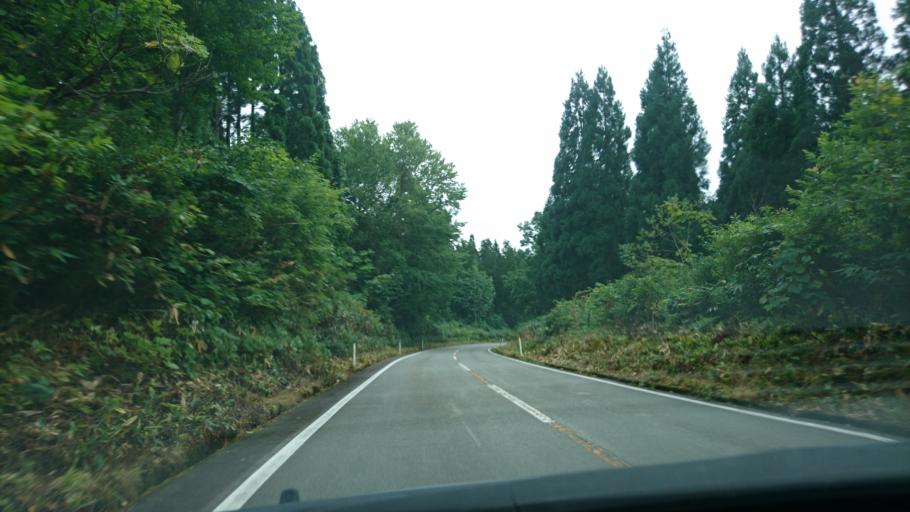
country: JP
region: Akita
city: Yuzawa
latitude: 38.9721
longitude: 140.7227
